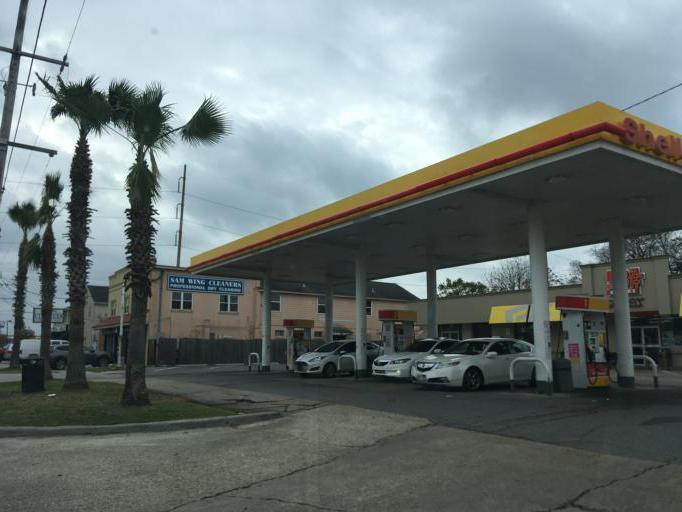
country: US
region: Louisiana
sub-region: Orleans Parish
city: New Orleans
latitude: 29.9897
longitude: -90.0587
